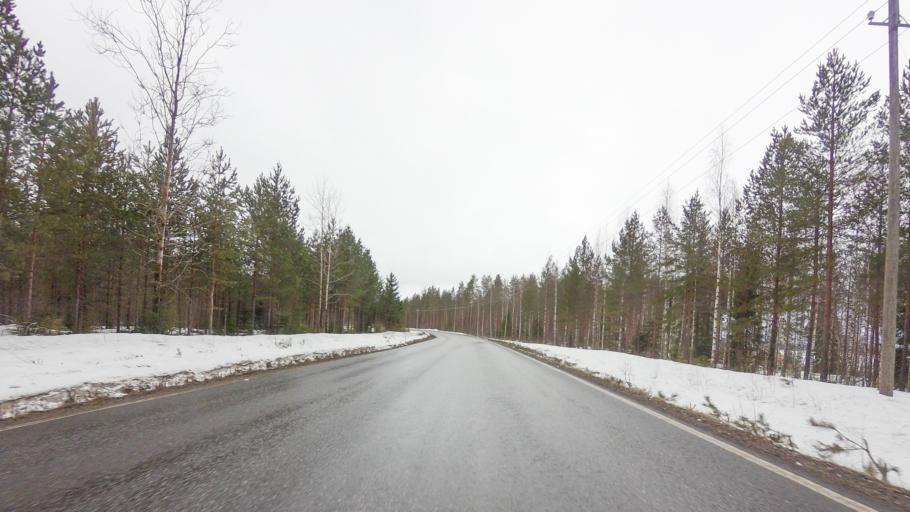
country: FI
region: Southern Savonia
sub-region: Savonlinna
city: Savonlinna
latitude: 61.9707
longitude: 28.8161
